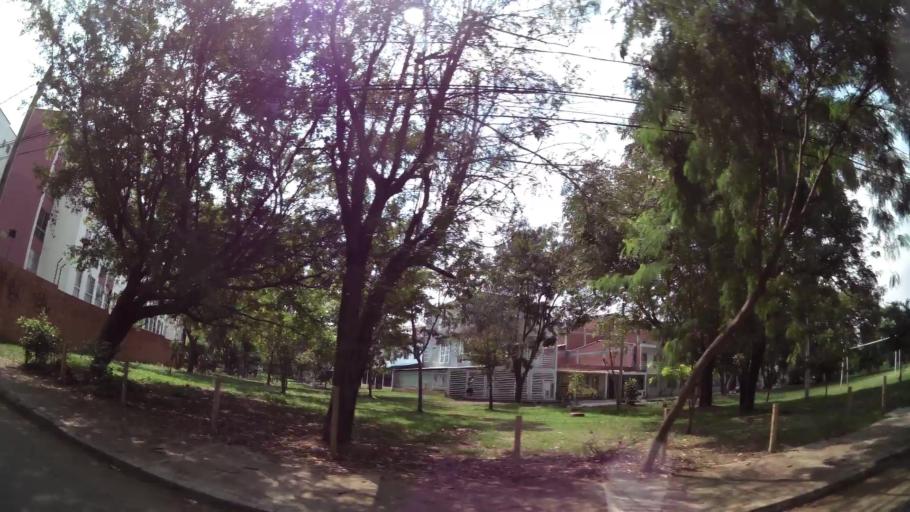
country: CO
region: Valle del Cauca
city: Cali
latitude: 3.4968
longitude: -76.5008
